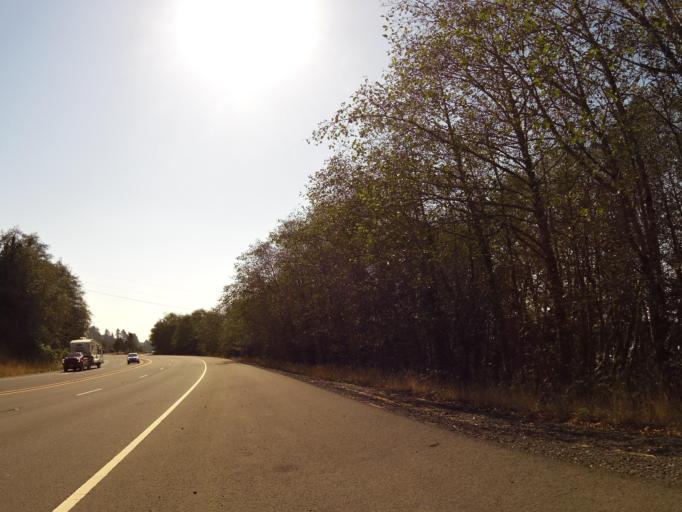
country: US
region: Oregon
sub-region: Tillamook County
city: Pacific City
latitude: 45.1448
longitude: -123.9686
